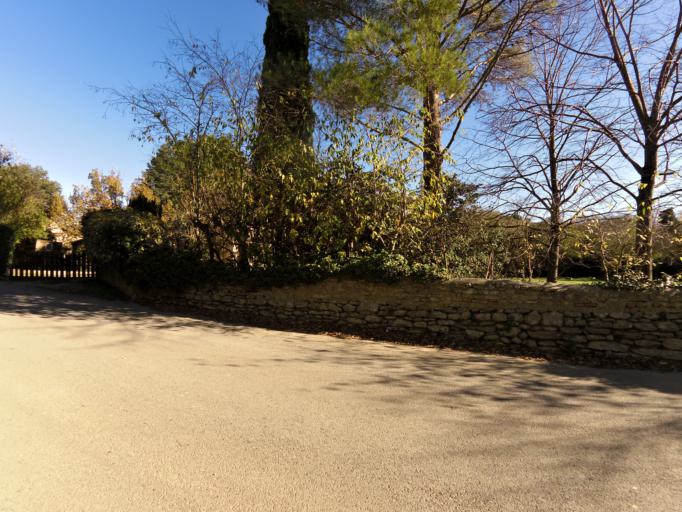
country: FR
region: Languedoc-Roussillon
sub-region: Departement du Gard
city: Aubais
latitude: 43.7562
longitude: 4.1431
